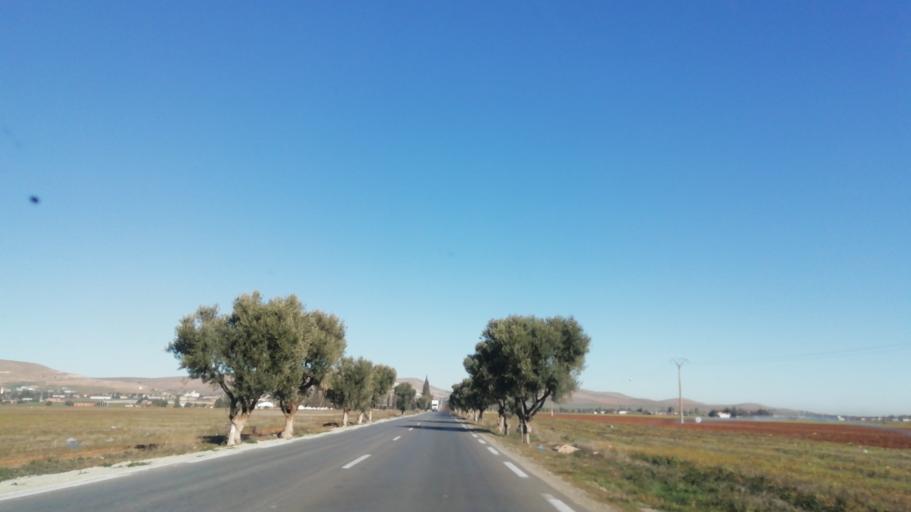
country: DZ
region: Mascara
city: Mascara
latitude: 35.2092
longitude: 0.1105
